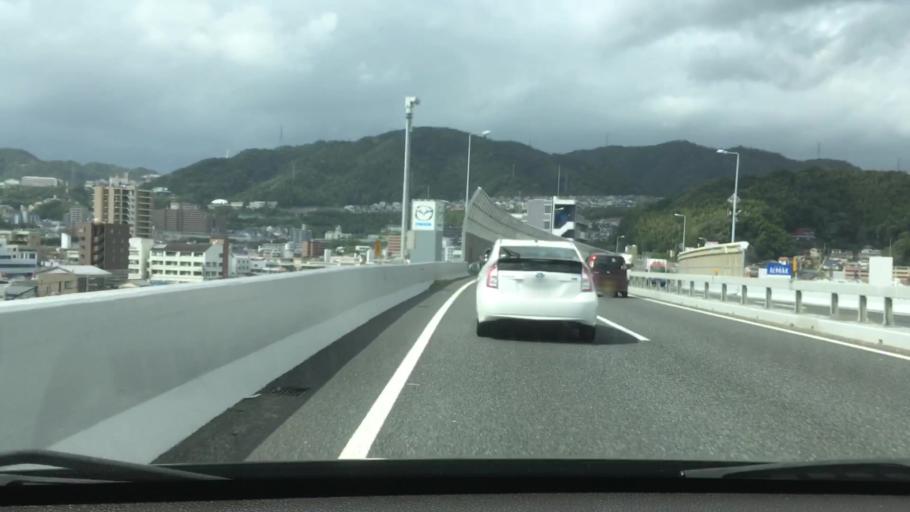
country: JP
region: Hiroshima
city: Hiroshima-shi
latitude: 34.3899
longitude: 132.4255
